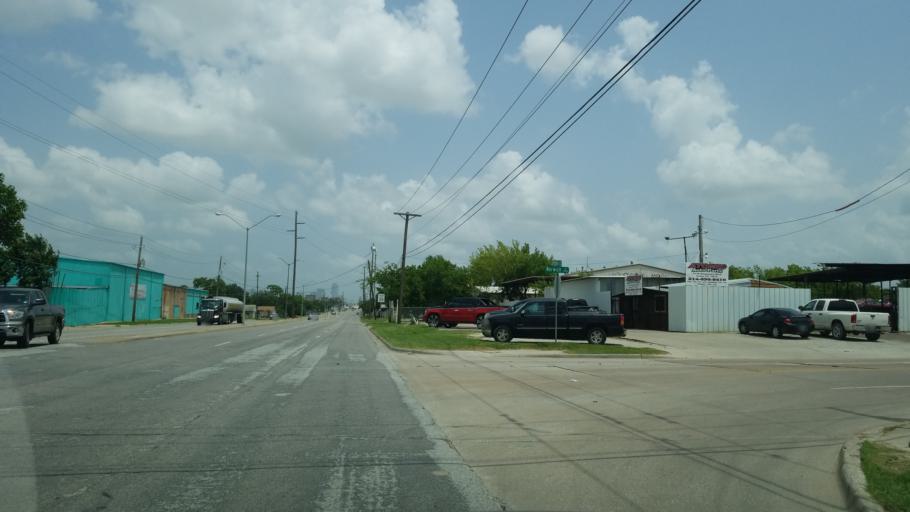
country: US
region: Texas
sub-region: Dallas County
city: Cockrell Hill
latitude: 32.7788
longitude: -96.8828
